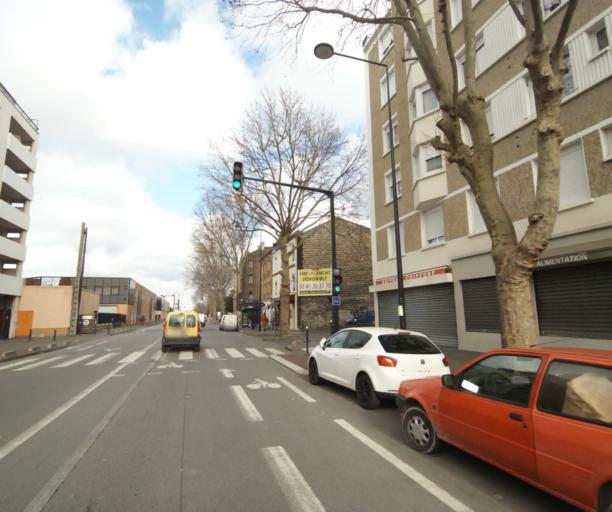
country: FR
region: Ile-de-France
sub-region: Departement de Seine-Saint-Denis
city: Saint-Denis
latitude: 48.9261
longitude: 2.3419
